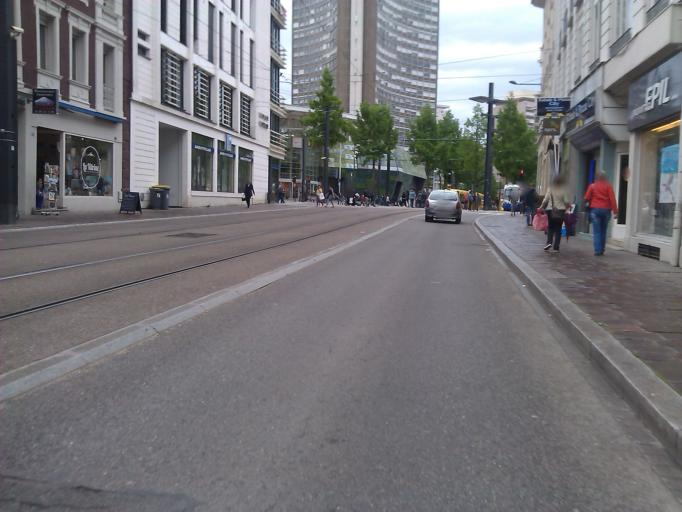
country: FR
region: Alsace
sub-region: Departement du Haut-Rhin
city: Mulhouse
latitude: 47.7498
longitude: 7.3379
